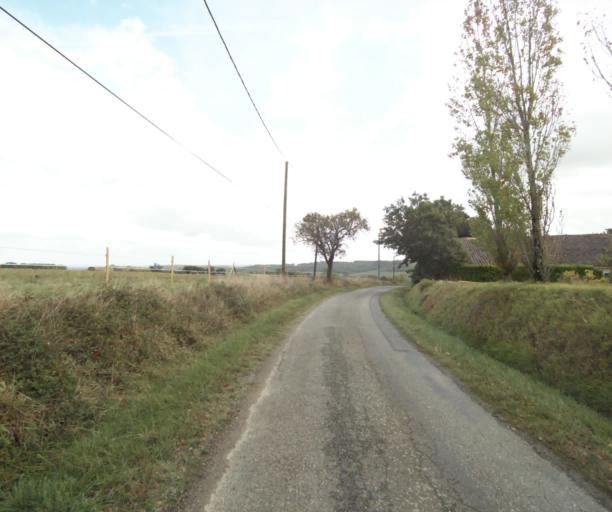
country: FR
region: Midi-Pyrenees
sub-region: Departement du Tarn-et-Garonne
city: Beaumont-de-Lomagne
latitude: 43.8714
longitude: 1.0993
